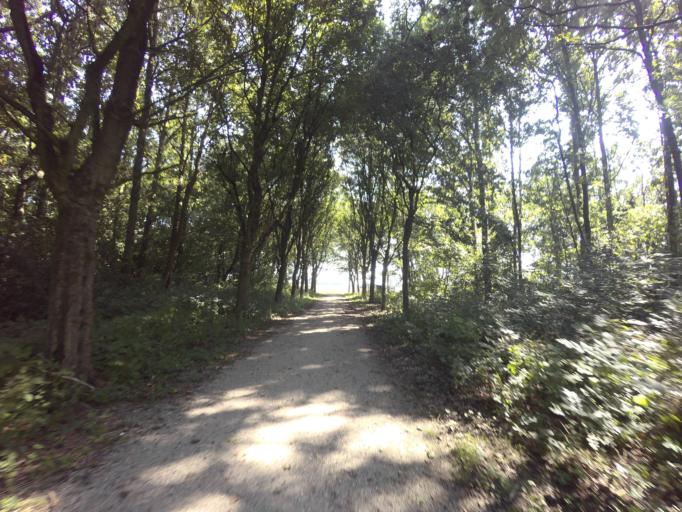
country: NL
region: Groningen
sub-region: Gemeente De Marne
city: Ulrum
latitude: 53.3591
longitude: 6.2932
